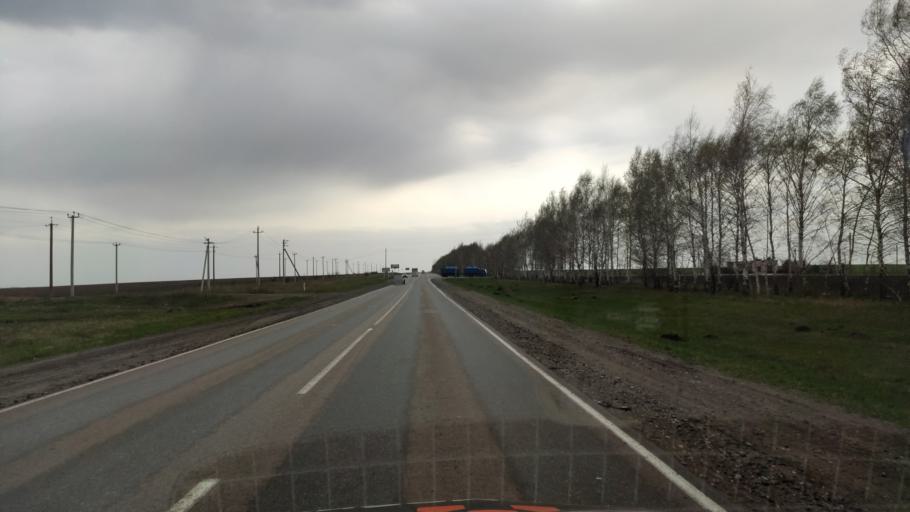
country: RU
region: Kursk
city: Gorshechnoye
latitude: 51.5091
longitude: 37.9993
